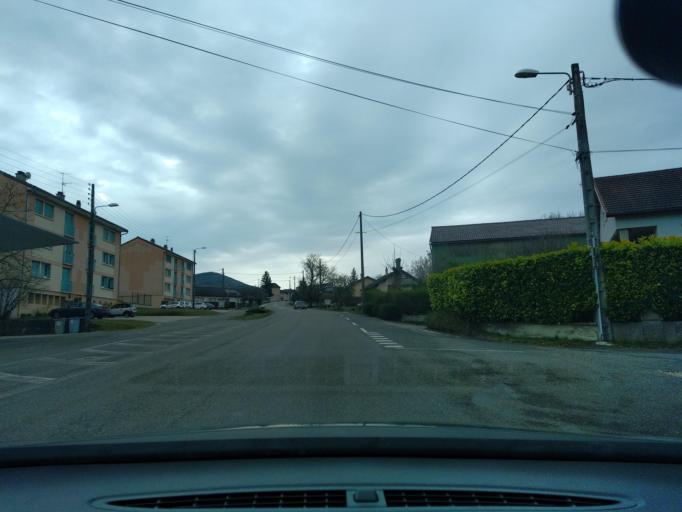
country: FR
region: Franche-Comte
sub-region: Departement du Jura
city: Arinthod
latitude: 46.3971
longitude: 5.5663
